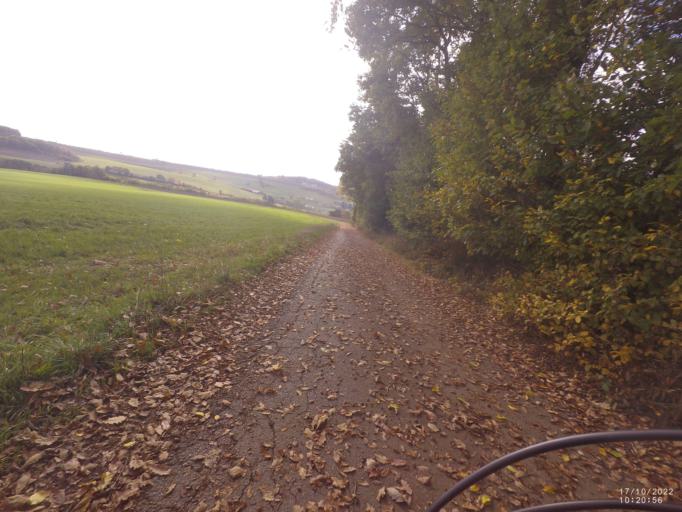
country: DE
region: Rheinland-Pfalz
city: Steiningen
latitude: 50.1947
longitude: 6.9156
